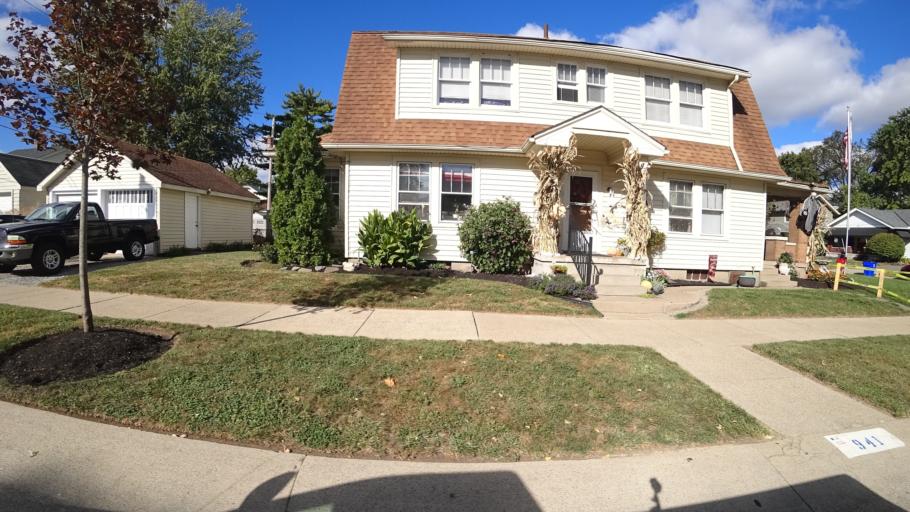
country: US
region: Ohio
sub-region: Butler County
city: Fairfield
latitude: 39.3658
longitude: -84.5512
